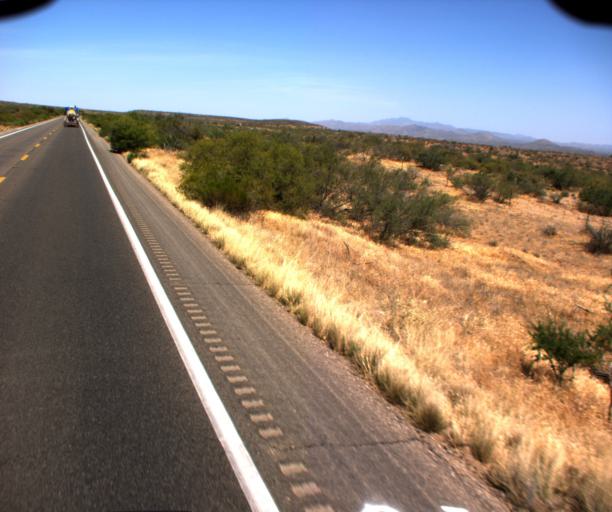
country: US
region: Arizona
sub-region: Gila County
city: Peridot
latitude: 33.3147
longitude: -110.5183
